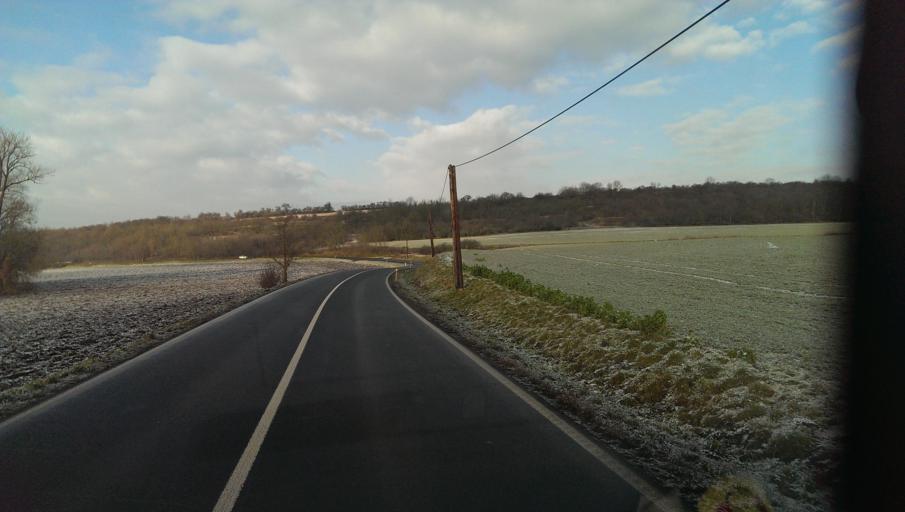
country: CZ
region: Ustecky
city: Budyne nad Ohri
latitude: 50.4123
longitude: 14.1100
